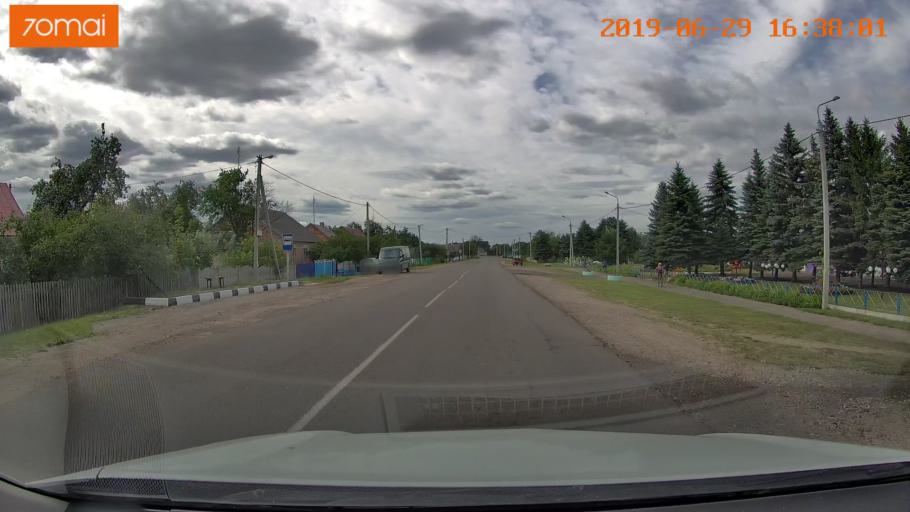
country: BY
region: Brest
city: Luninyets
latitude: 52.2302
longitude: 27.0186
